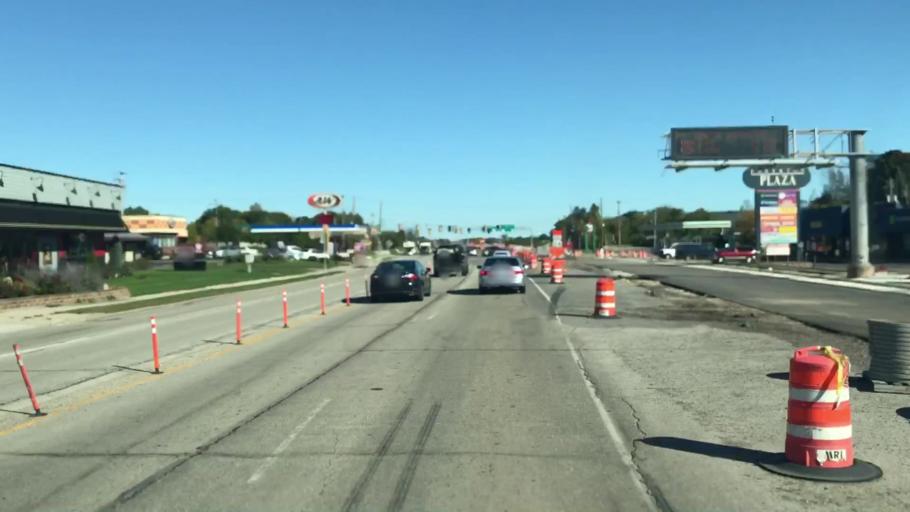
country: US
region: Wisconsin
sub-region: Milwaukee County
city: Hales Corners
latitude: 42.9501
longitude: -88.0482
